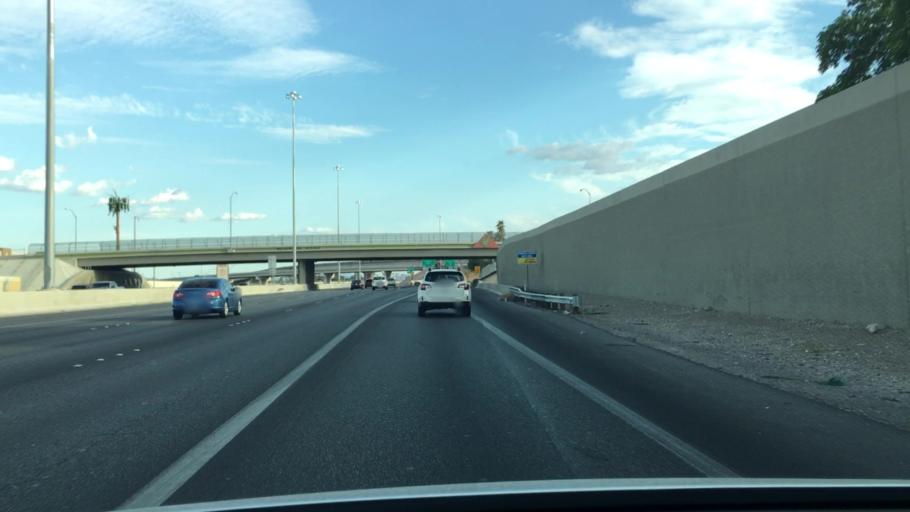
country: US
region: Nevada
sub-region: Clark County
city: Spring Valley
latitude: 36.1827
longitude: -115.2447
